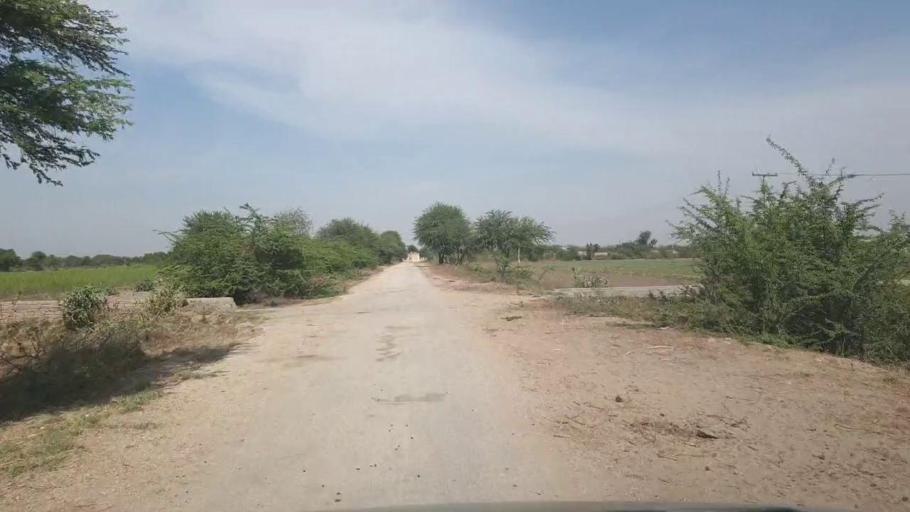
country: PK
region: Sindh
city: Kunri
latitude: 25.1961
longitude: 69.6873
